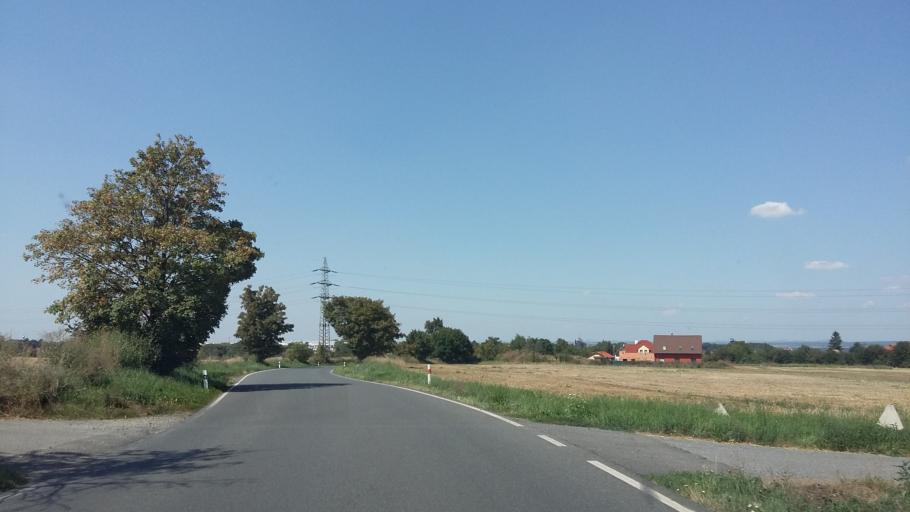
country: CZ
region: Central Bohemia
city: Zelenec
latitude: 50.1585
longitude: 14.6828
